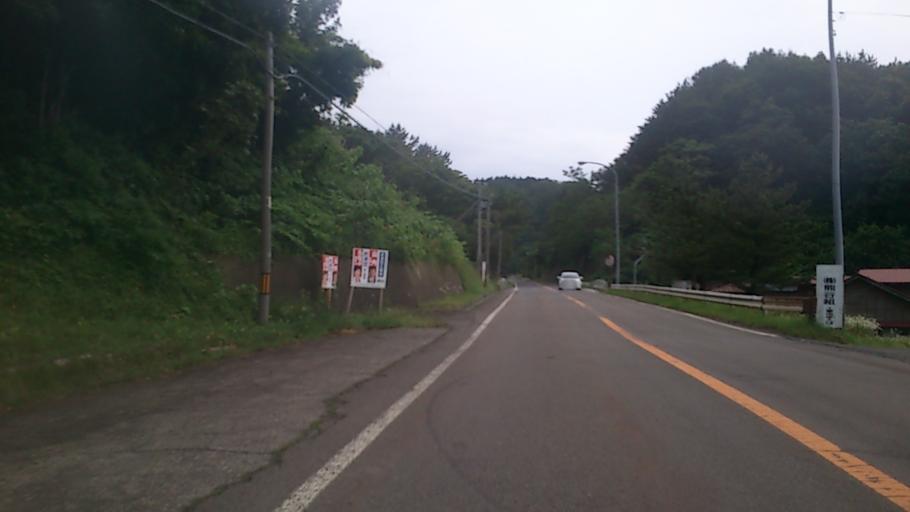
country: JP
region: Akita
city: Noshiromachi
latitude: 40.4896
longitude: 139.9500
